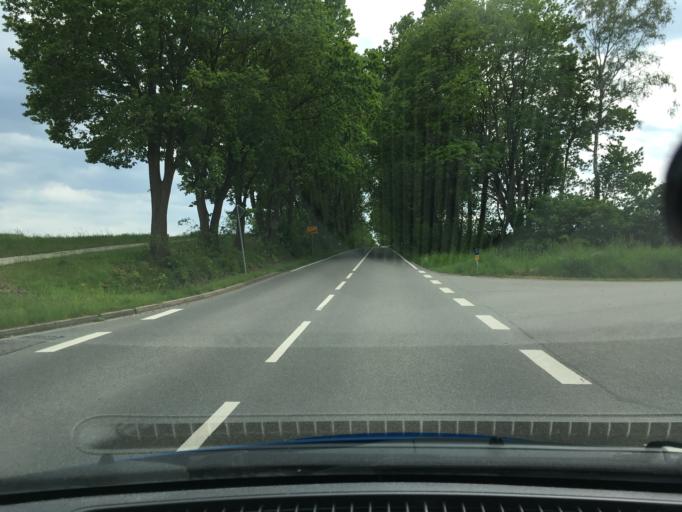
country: DE
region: Lower Saxony
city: Betzendorf
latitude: 53.1351
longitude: 10.3100
